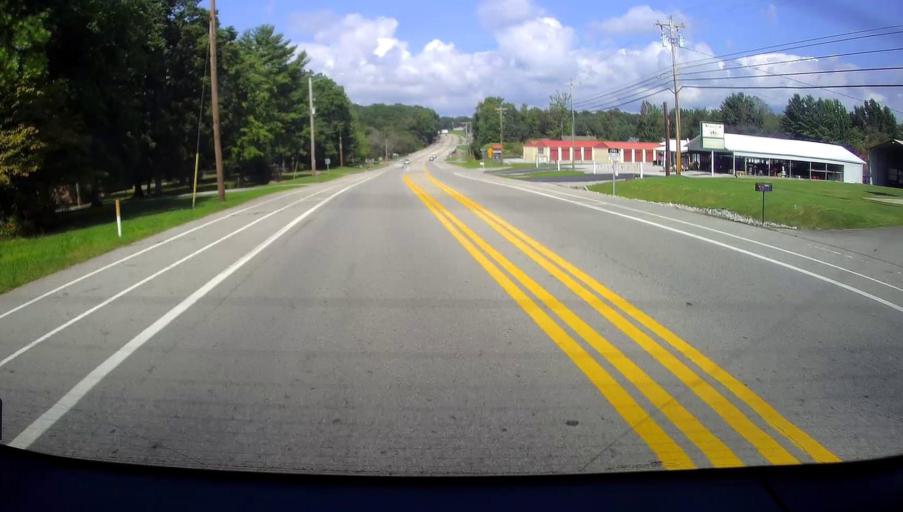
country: US
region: Tennessee
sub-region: Coffee County
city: Manchester
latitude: 35.4931
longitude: -86.1005
